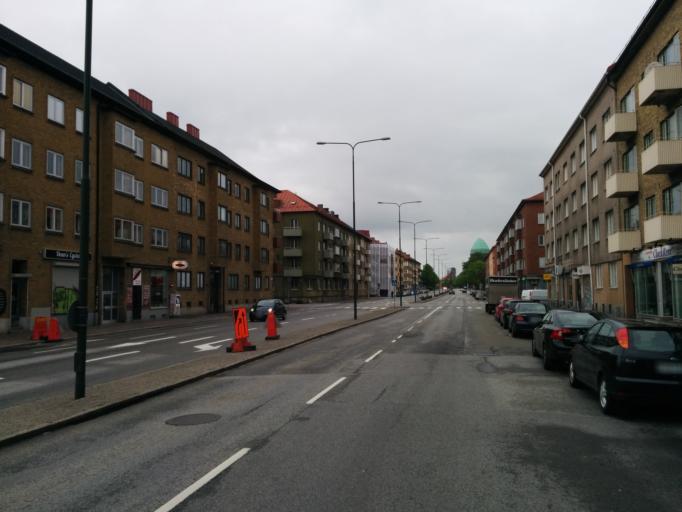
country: SE
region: Skane
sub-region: Malmo
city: Malmoe
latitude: 55.5921
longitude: 13.0189
